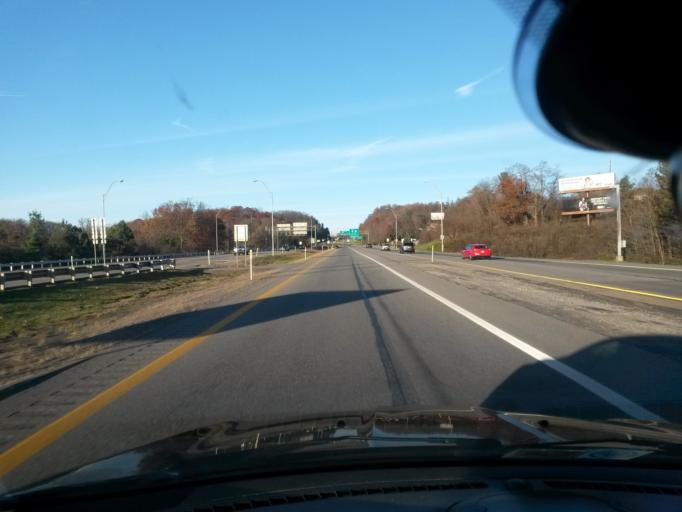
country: US
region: West Virginia
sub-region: Raleigh County
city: Prosperity
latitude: 37.8375
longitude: -81.2138
